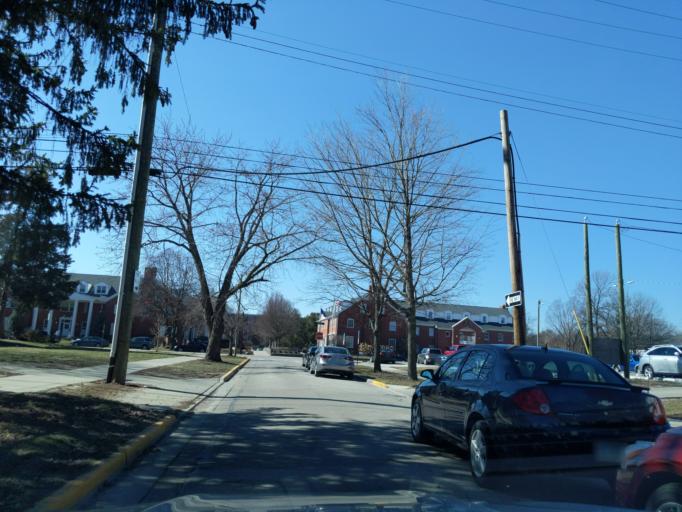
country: US
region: Indiana
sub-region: Tippecanoe County
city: West Lafayette
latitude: 40.4293
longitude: -86.9183
